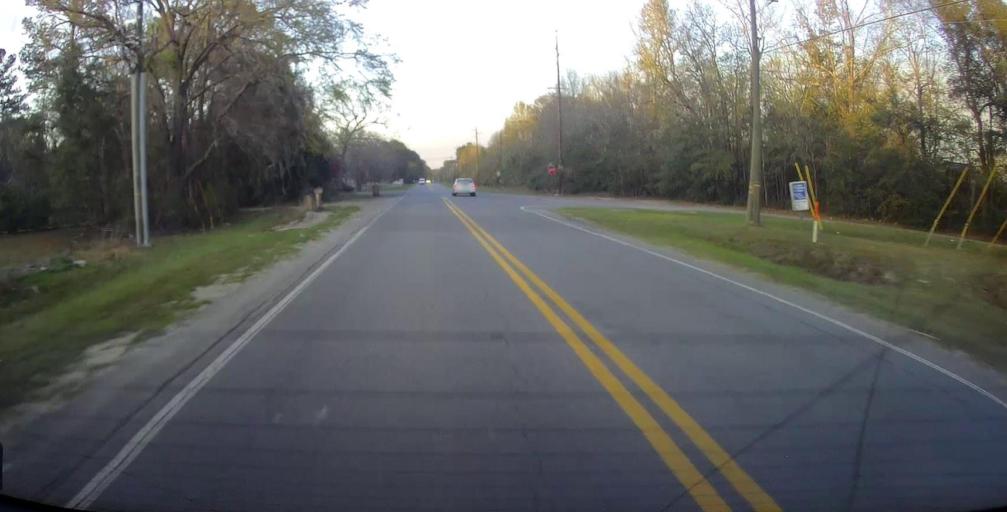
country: US
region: Georgia
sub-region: Chatham County
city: Bloomingdale
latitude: 32.1518
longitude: -81.3885
